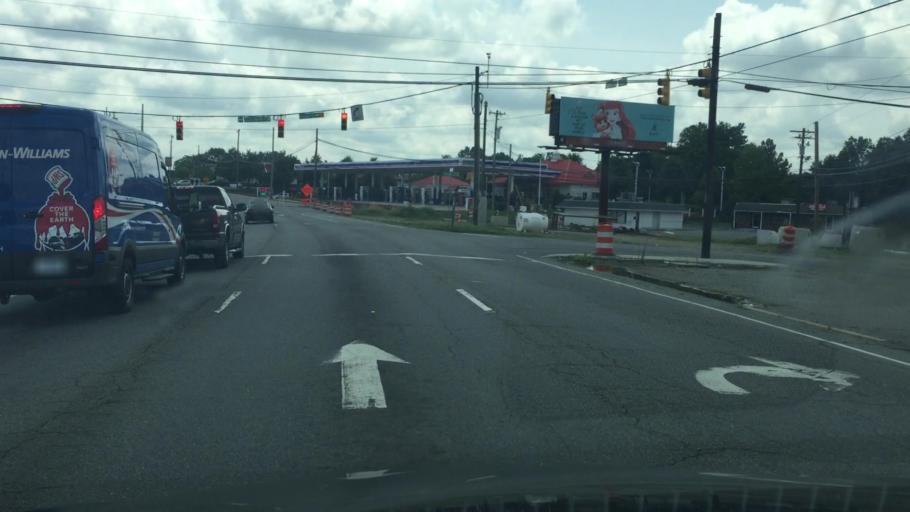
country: US
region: North Carolina
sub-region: Cabarrus County
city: Concord
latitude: 35.4419
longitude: -80.6084
